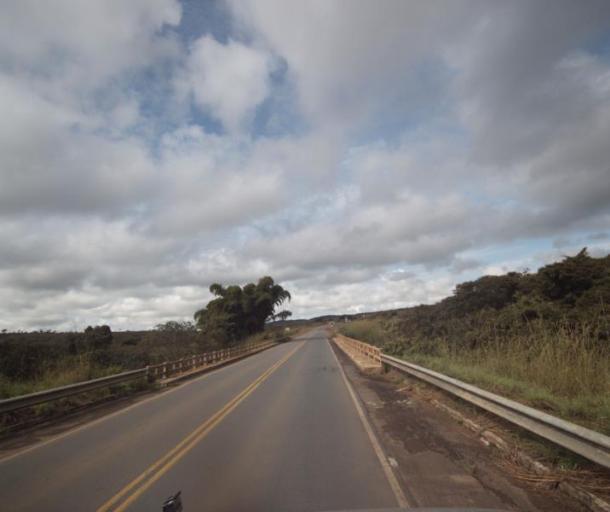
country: BR
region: Goias
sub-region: Pirenopolis
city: Pirenopolis
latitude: -15.8232
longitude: -48.7784
